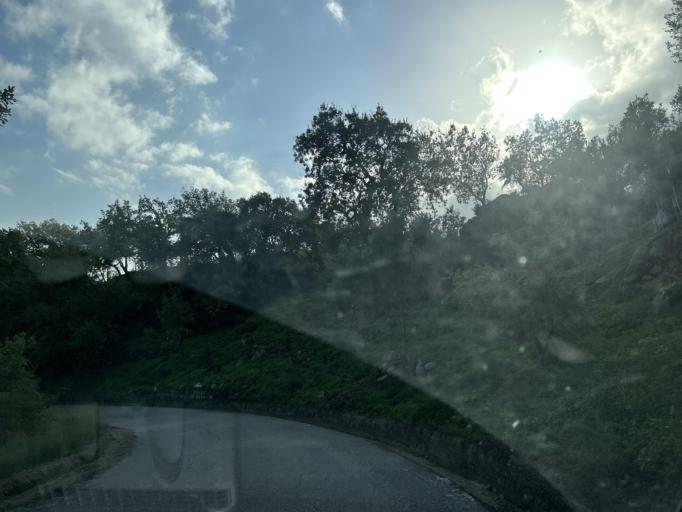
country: IT
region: Calabria
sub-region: Provincia di Catanzaro
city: Montepaone
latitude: 38.7174
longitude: 16.5099
